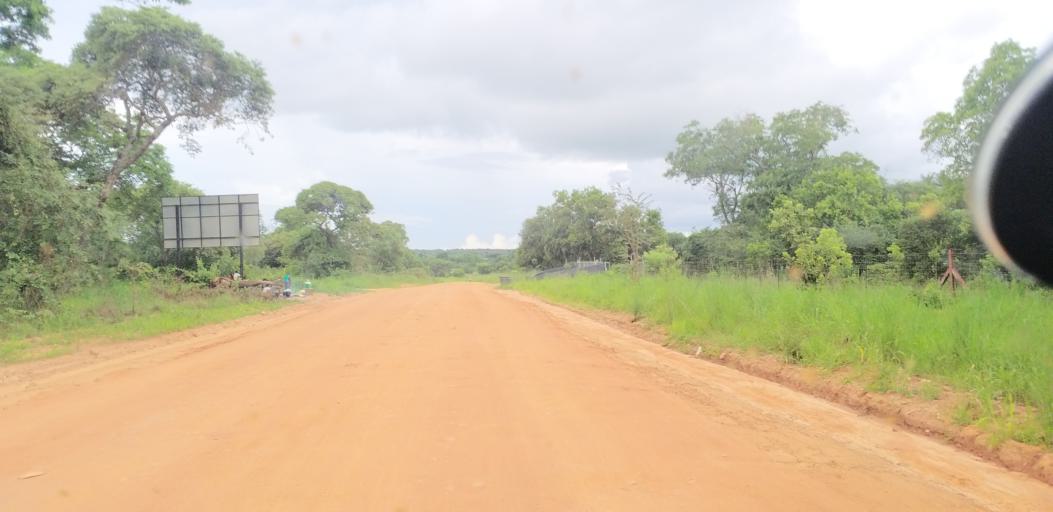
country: ZM
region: Lusaka
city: Lusaka
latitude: -15.1980
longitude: 28.4410
